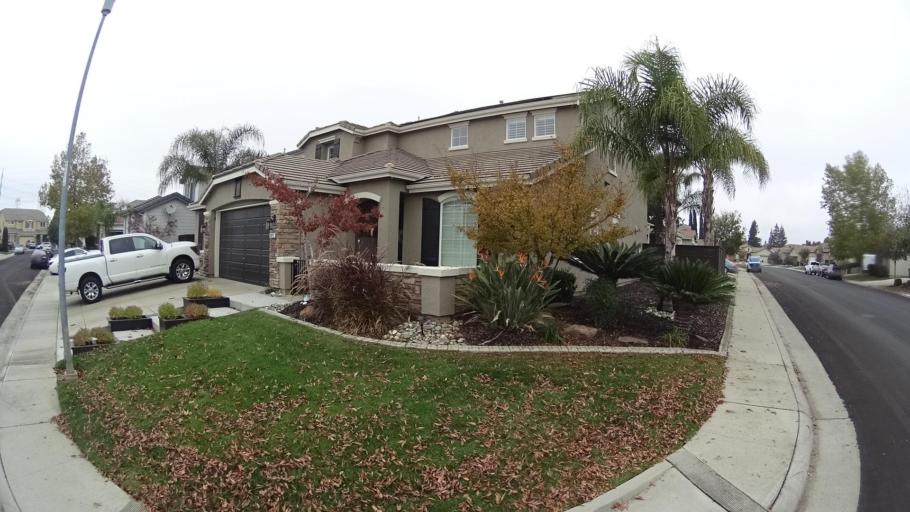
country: US
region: California
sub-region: Sacramento County
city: Elk Grove
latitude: 38.3905
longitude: -121.3486
